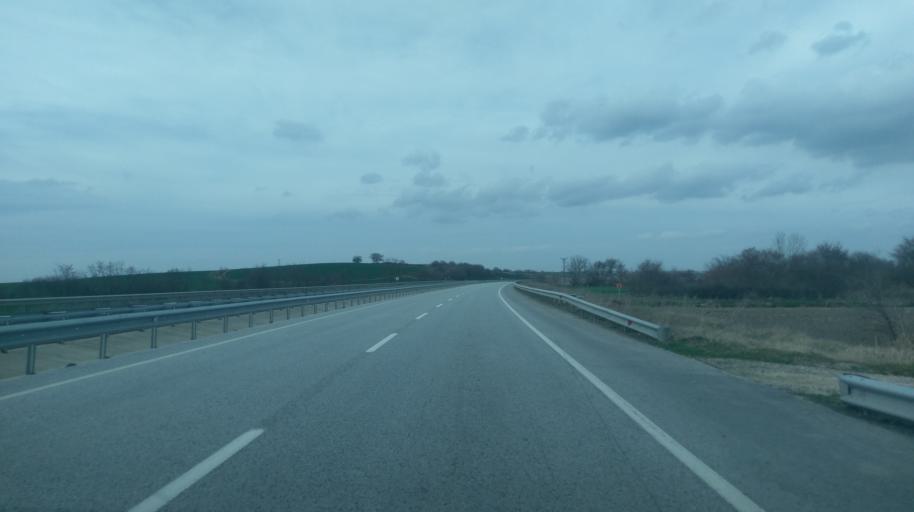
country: TR
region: Edirne
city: Havsa
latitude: 41.4774
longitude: 26.8166
